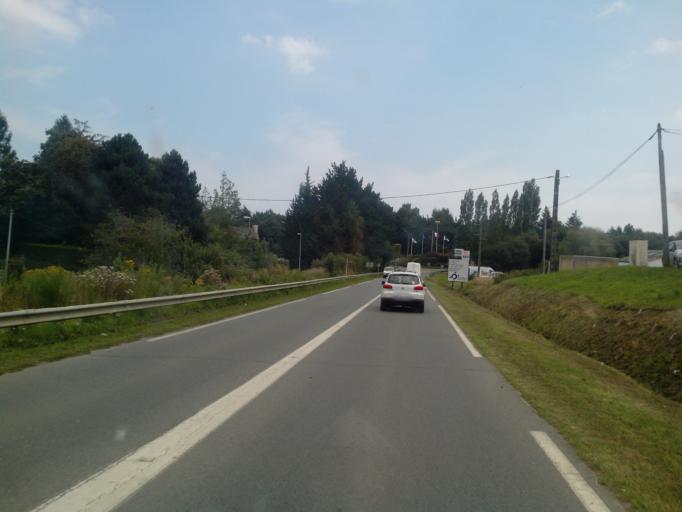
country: FR
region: Brittany
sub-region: Departement des Cotes-d'Armor
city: Plouha
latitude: 48.6687
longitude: -2.9246
